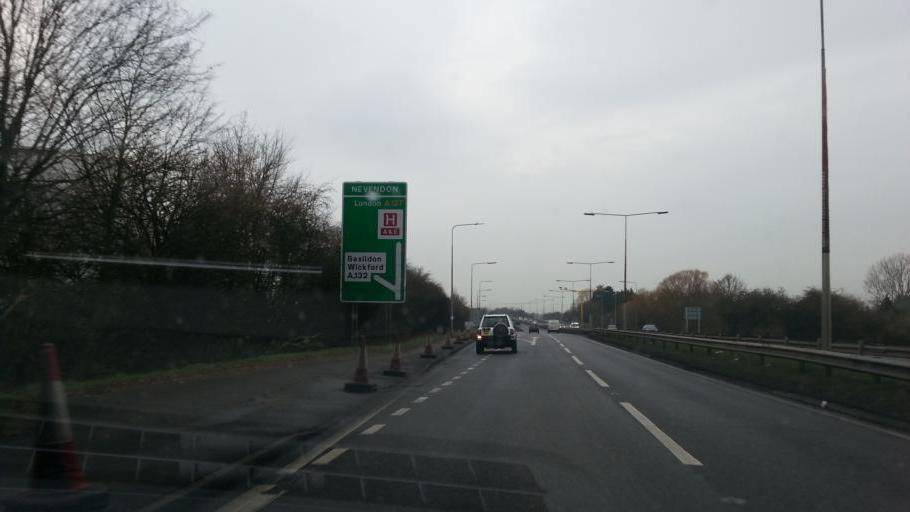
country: GB
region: England
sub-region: Essex
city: Wickford
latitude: 51.5918
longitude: 0.5097
